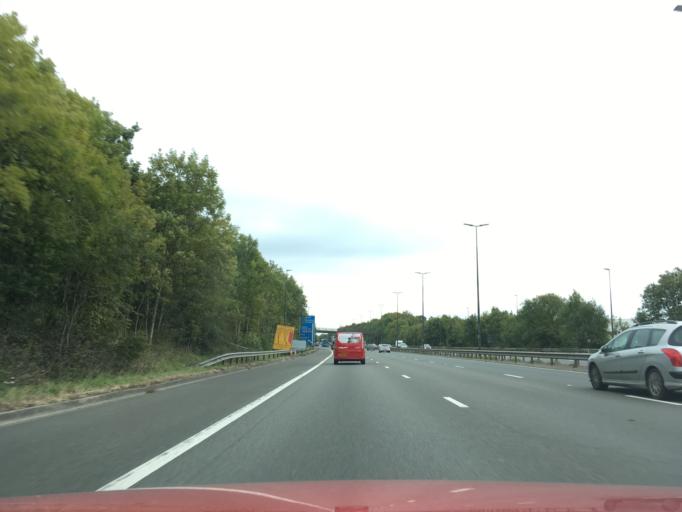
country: GB
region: Wales
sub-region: Newport
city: Marshfield
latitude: 51.5584
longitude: -3.0457
